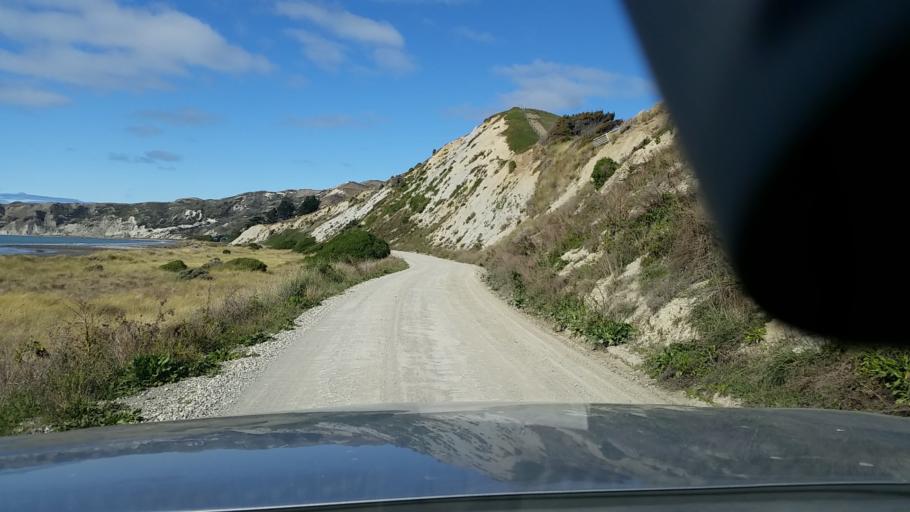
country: NZ
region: Marlborough
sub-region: Marlborough District
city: Blenheim
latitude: -41.7229
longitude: 174.1977
